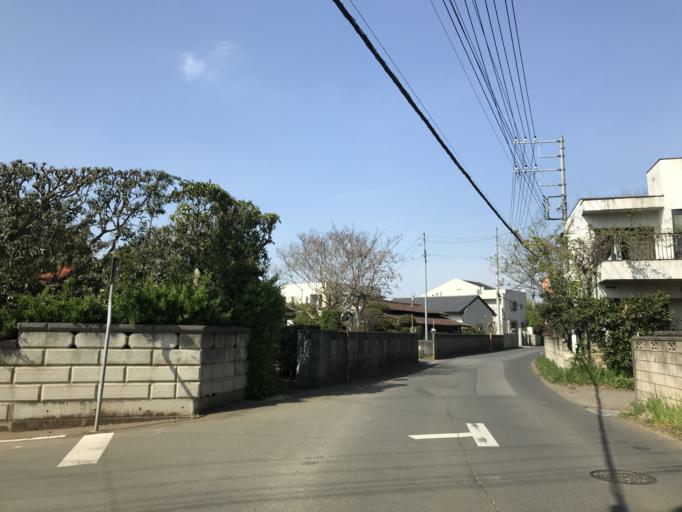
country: JP
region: Ibaraki
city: Mitsukaido
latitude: 35.9736
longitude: 139.9524
